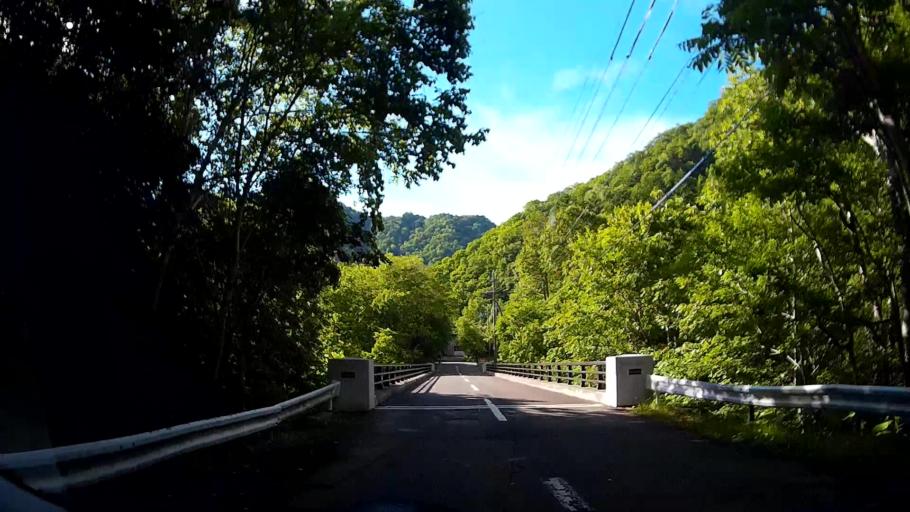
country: JP
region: Hokkaido
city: Sapporo
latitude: 42.9811
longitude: 141.1600
